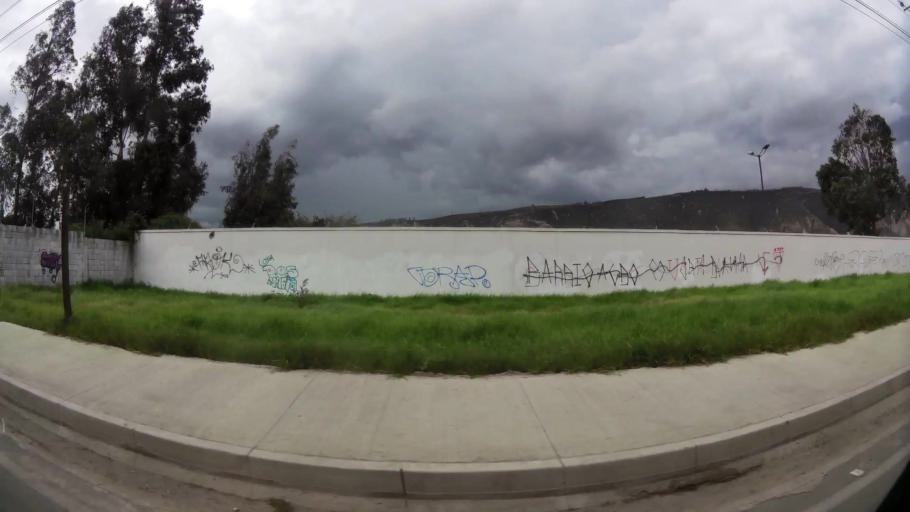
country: EC
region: Pichincha
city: Quito
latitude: -0.0202
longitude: -78.4523
